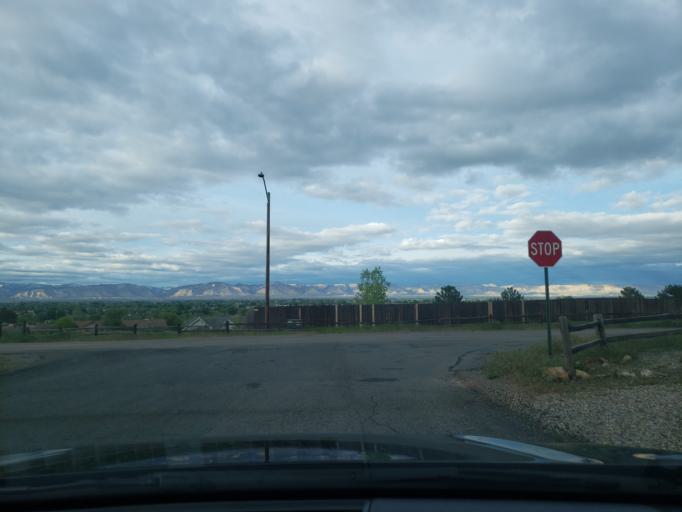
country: US
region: Colorado
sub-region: Mesa County
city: Fruita
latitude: 39.1383
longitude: -108.7421
